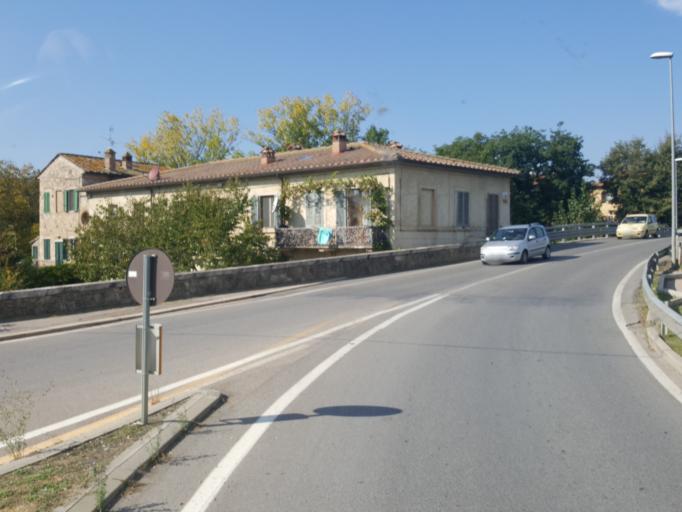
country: IT
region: Tuscany
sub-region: Provincia di Siena
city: Colle di Val d'Elsa
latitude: 43.4033
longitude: 11.1346
